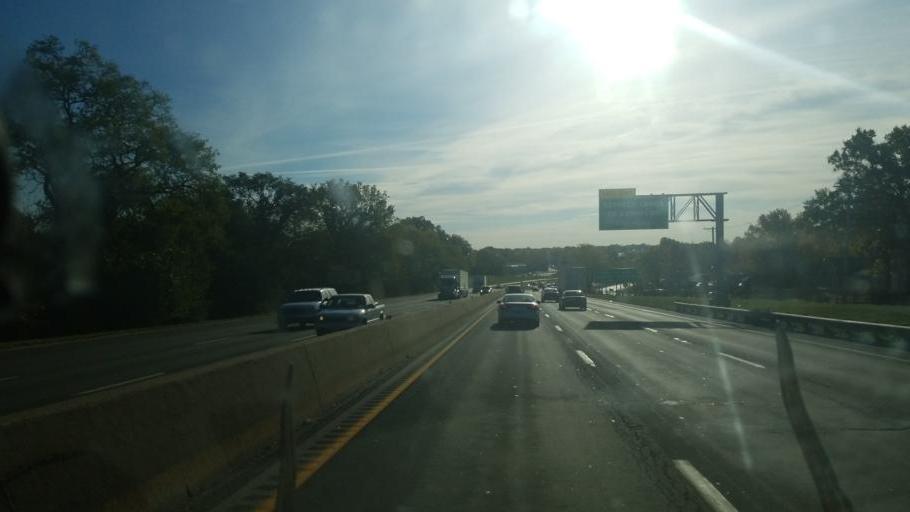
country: US
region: Missouri
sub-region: Saint Louis County
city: Northwoods
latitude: 38.7070
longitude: -90.2750
